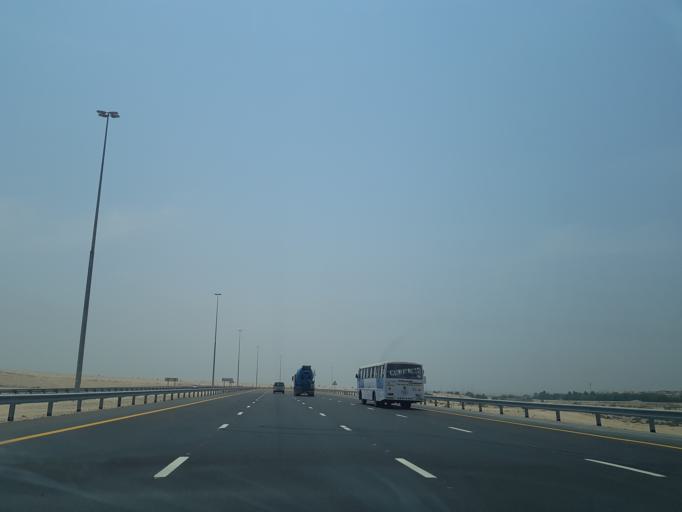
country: AE
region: Dubai
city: Dubai
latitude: 25.0130
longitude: 55.2191
